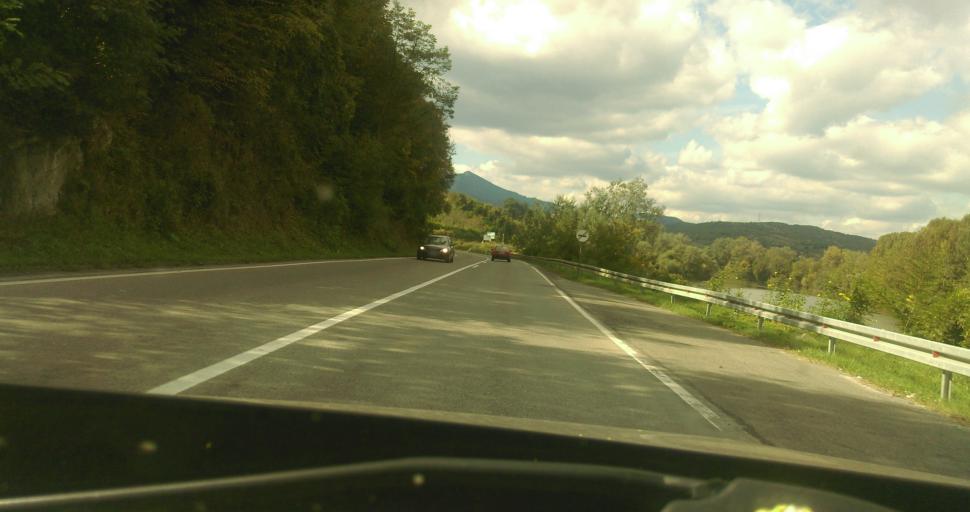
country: RS
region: Central Serbia
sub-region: Moravicki Okrug
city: Cacak
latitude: 43.8962
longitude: 20.2864
